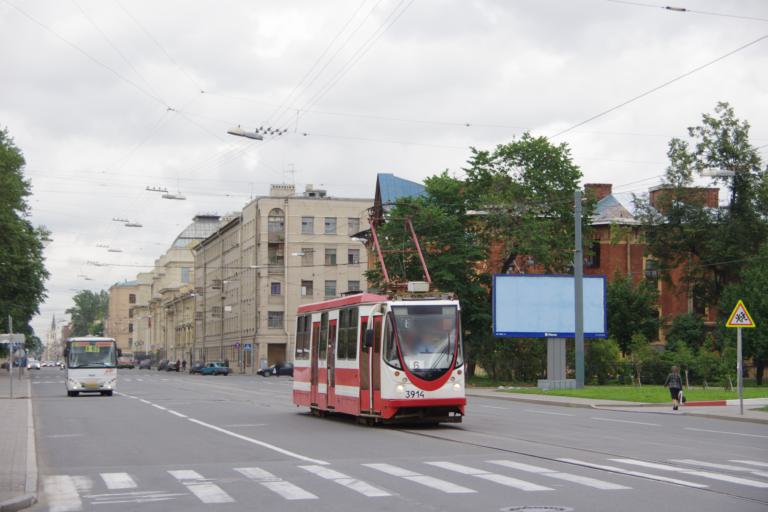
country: RU
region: St.-Petersburg
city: Vasyl'evsky Ostrov
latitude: 59.9366
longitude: 30.2556
